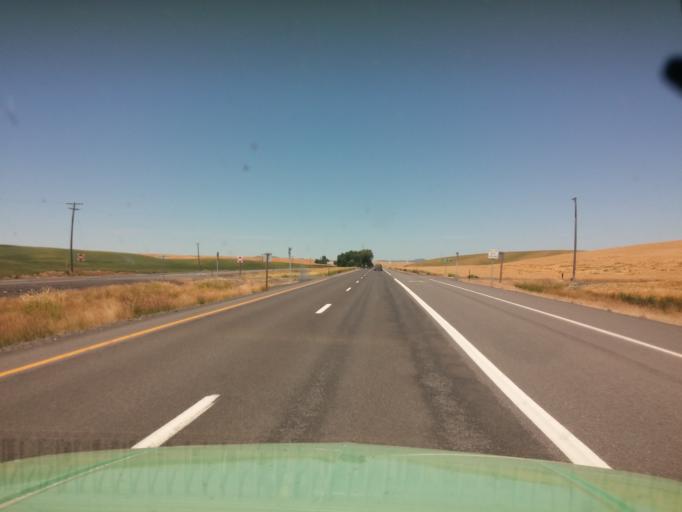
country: US
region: Idaho
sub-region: Nez Perce County
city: Lewiston
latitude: 46.5632
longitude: -116.9487
